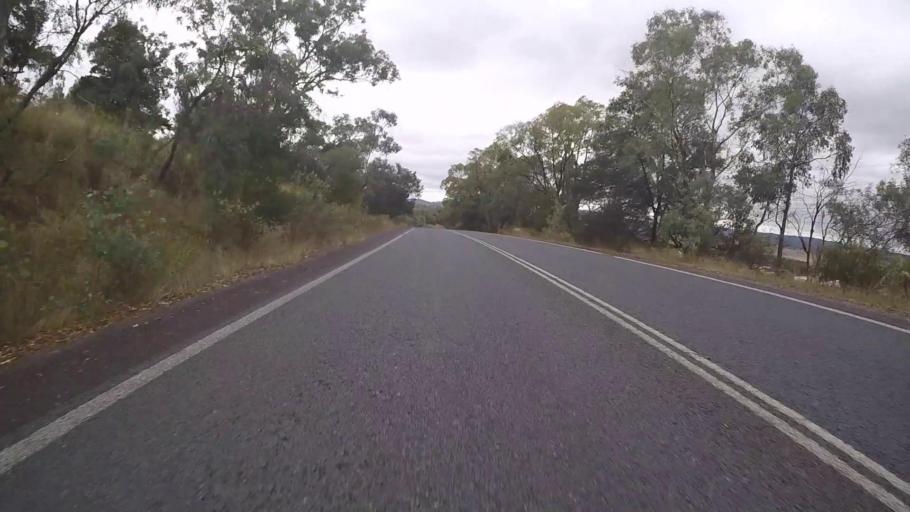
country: AU
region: Australian Capital Territory
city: Canberra
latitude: -35.2938
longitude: 149.1610
